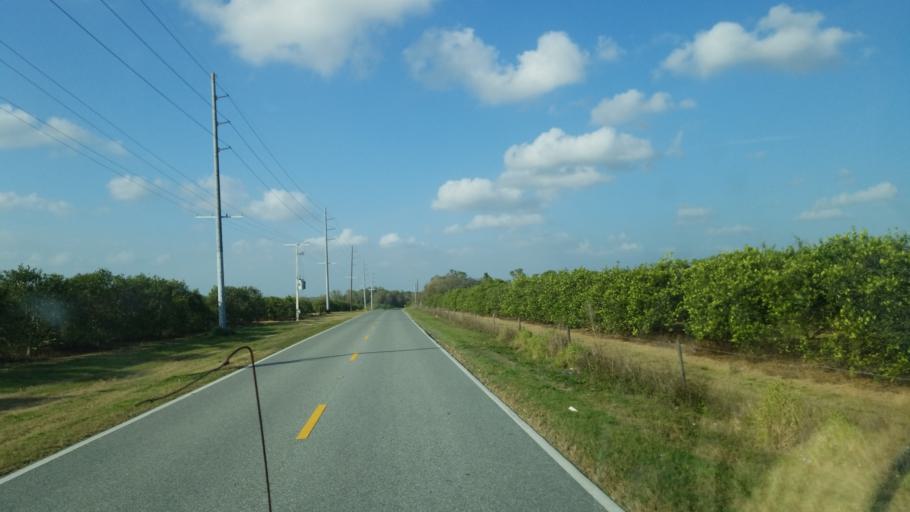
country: US
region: Florida
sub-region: Hardee County
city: Bowling Green
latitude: 27.5987
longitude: -81.9448
